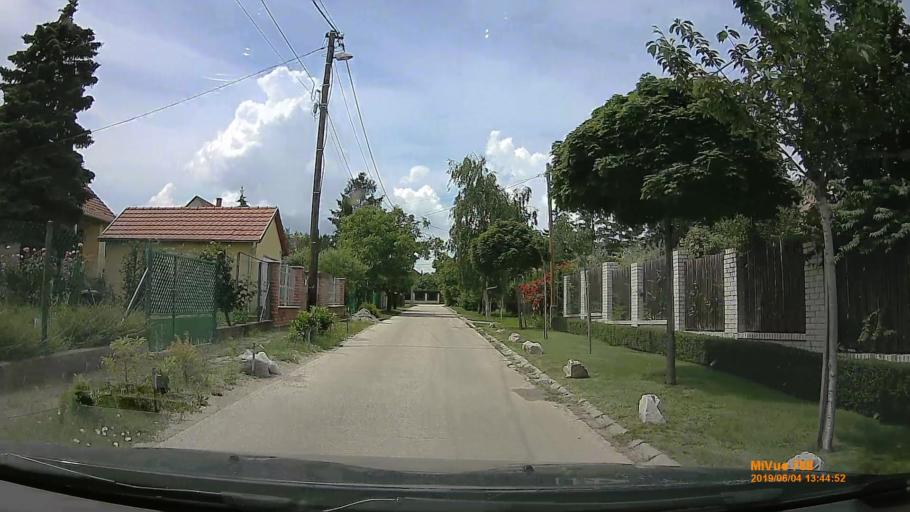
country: HU
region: Budapest
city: Budapest XXII. keruelet
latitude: 47.4298
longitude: 19.0007
